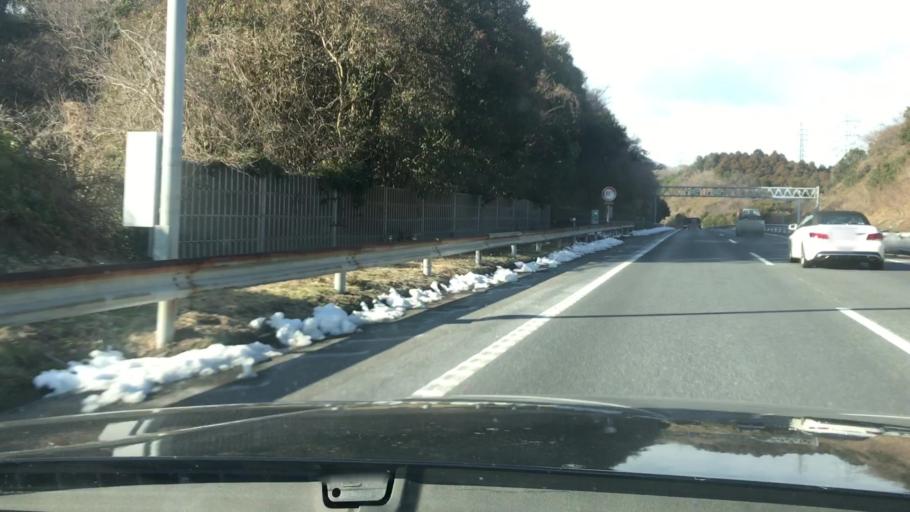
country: JP
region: Kanagawa
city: Zushi
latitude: 35.2968
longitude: 139.6174
